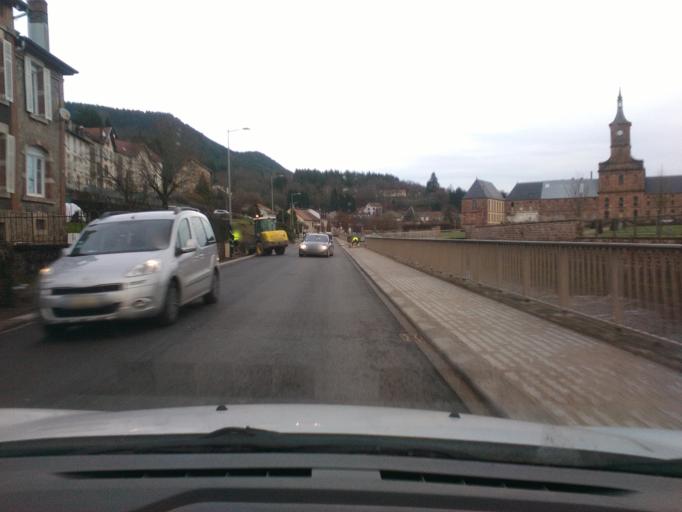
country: FR
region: Lorraine
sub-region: Departement des Vosges
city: Moyenmoutier
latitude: 48.3780
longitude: 6.9082
